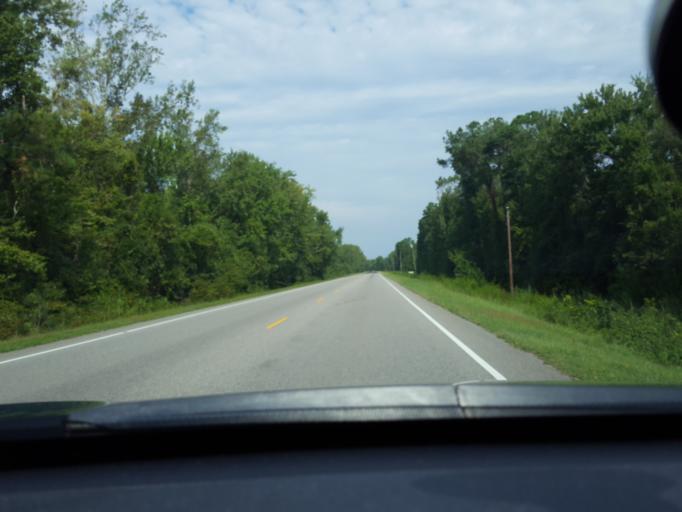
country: US
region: North Carolina
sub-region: Washington County
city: Plymouth
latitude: 35.9027
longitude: -76.7113
